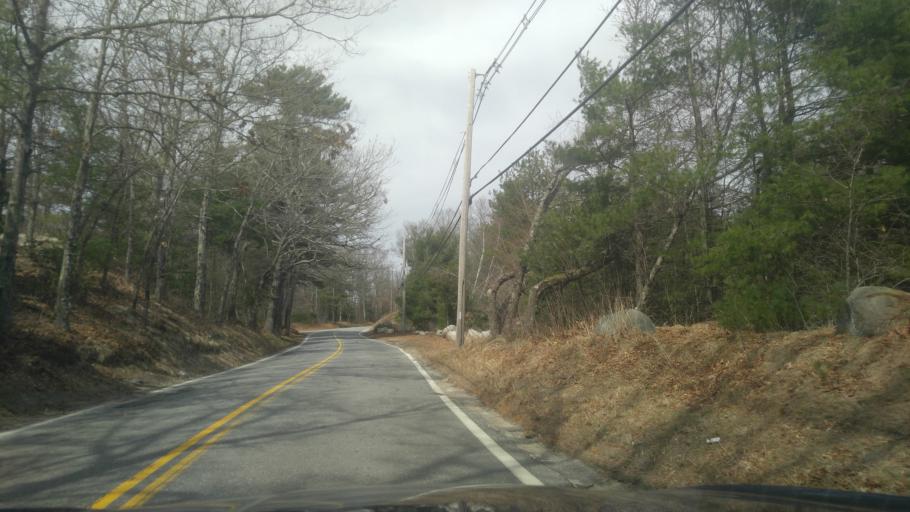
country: US
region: Rhode Island
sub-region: Kent County
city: West Warwick
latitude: 41.6446
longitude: -71.5736
